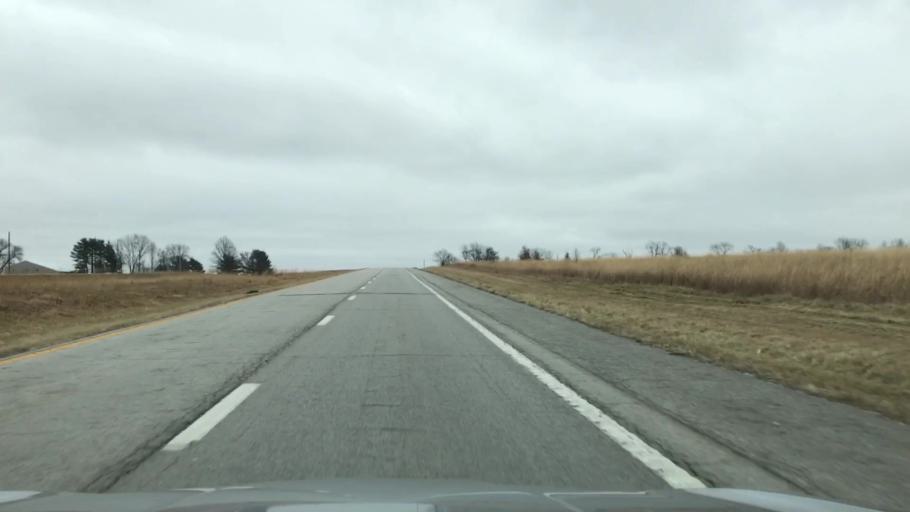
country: US
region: Missouri
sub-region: Linn County
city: Brookfield
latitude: 39.7785
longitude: -93.1601
